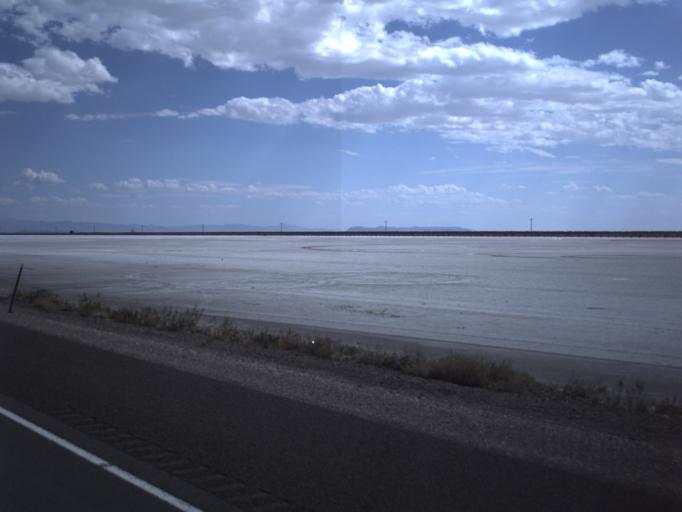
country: US
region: Utah
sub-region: Tooele County
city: Wendover
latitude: 40.7349
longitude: -113.6781
